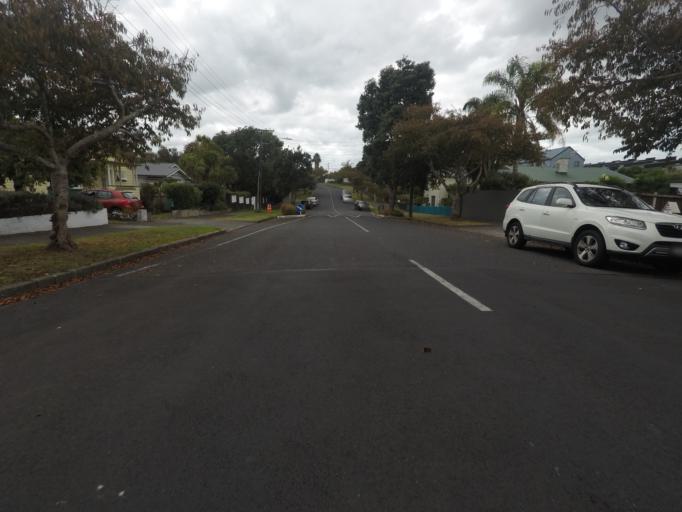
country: NZ
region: Auckland
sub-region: Auckland
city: Auckland
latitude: -36.8752
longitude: 174.7219
